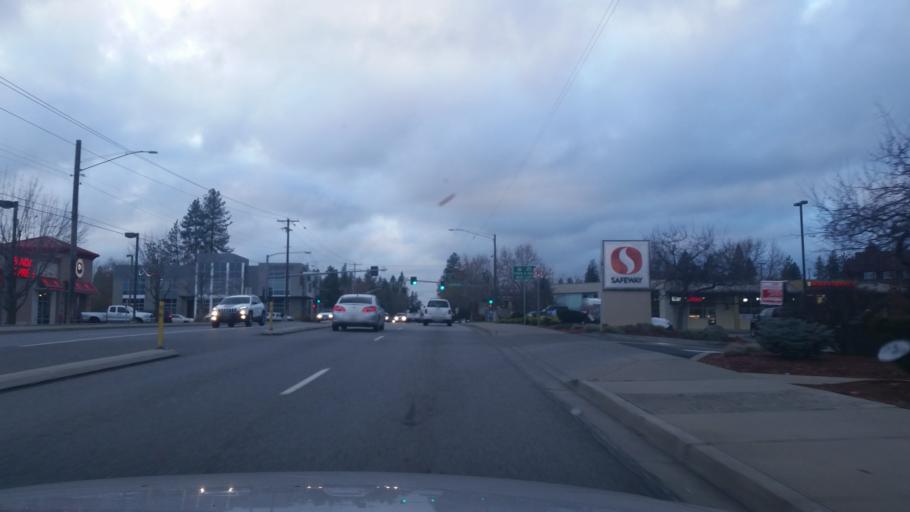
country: US
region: Washington
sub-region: Spokane County
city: Spokane
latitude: 47.6283
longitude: -117.3738
